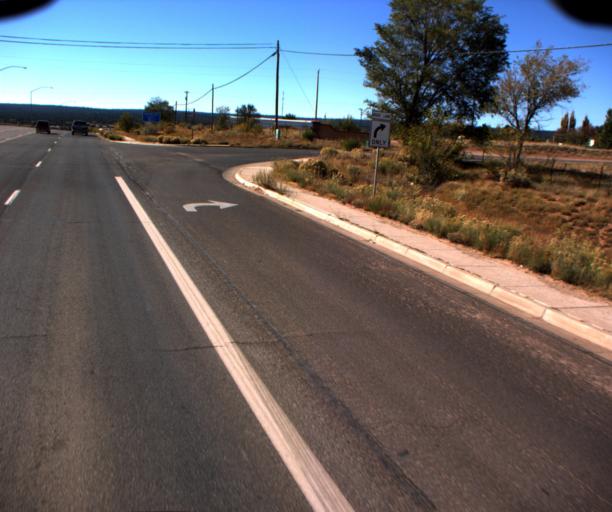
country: US
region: Arizona
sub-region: Apache County
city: Saint Michaels
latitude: 35.6557
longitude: -109.0977
